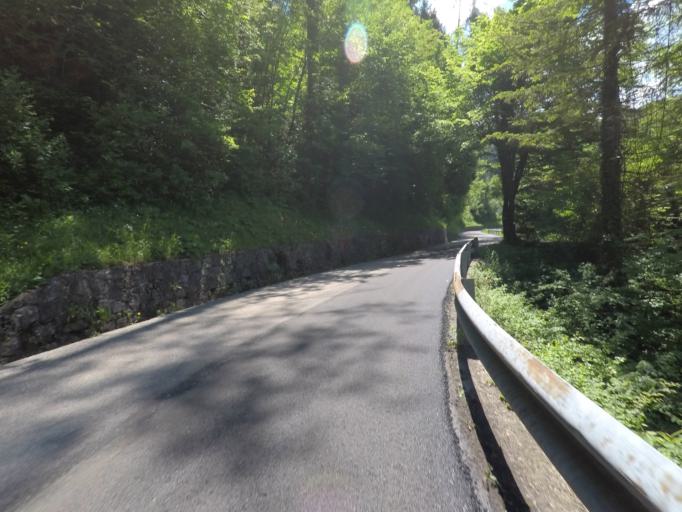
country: IT
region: Friuli Venezia Giulia
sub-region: Provincia di Udine
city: Raveo
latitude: 46.4352
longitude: 12.8878
